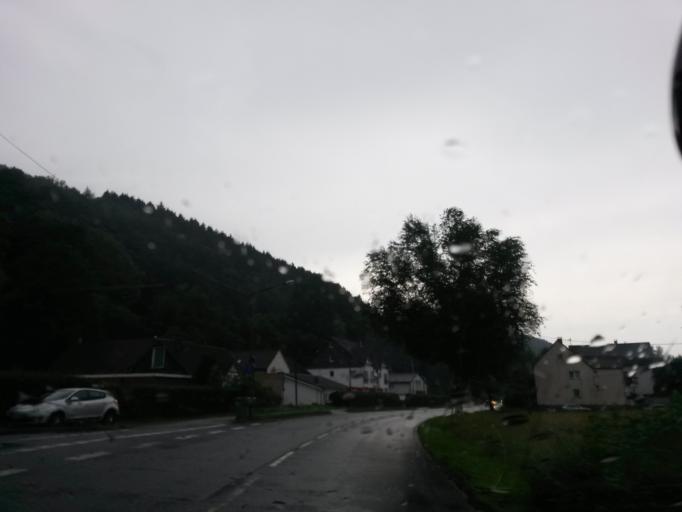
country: DE
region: North Rhine-Westphalia
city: Wiehl
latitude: 50.9937
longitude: 7.5025
